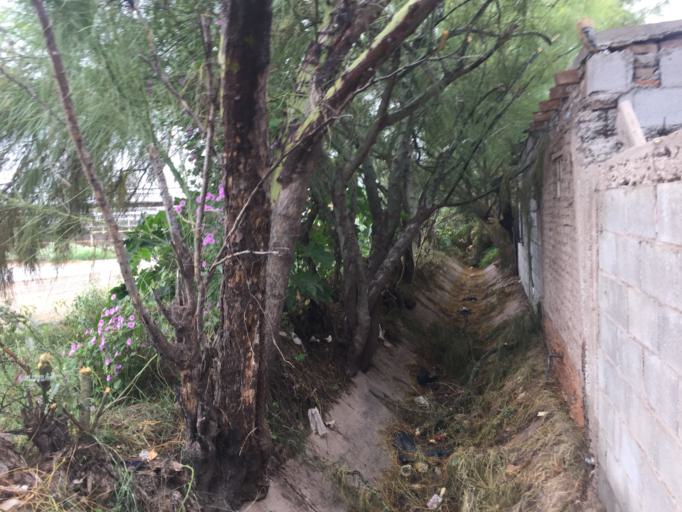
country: MX
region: Coahuila
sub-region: Matamoros
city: Veinte de Noviembre
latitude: 25.7230
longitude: -103.3610
